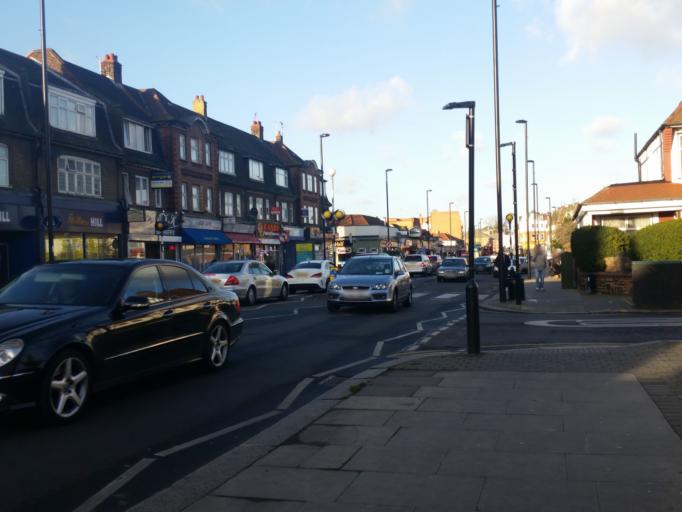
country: GB
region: England
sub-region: Greater London
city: Wood Green
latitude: 51.6095
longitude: -0.1098
